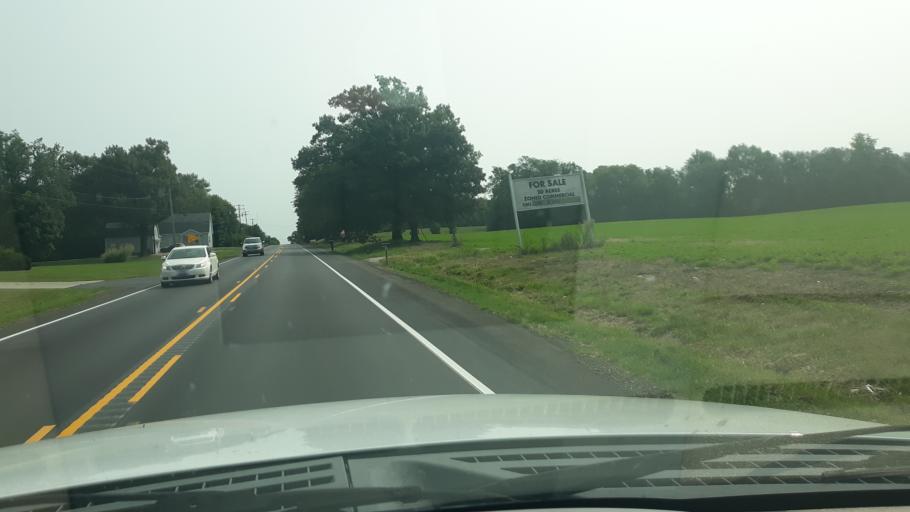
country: US
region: Indiana
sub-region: Gibson County
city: Princeton
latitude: 38.3556
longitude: -87.6206
